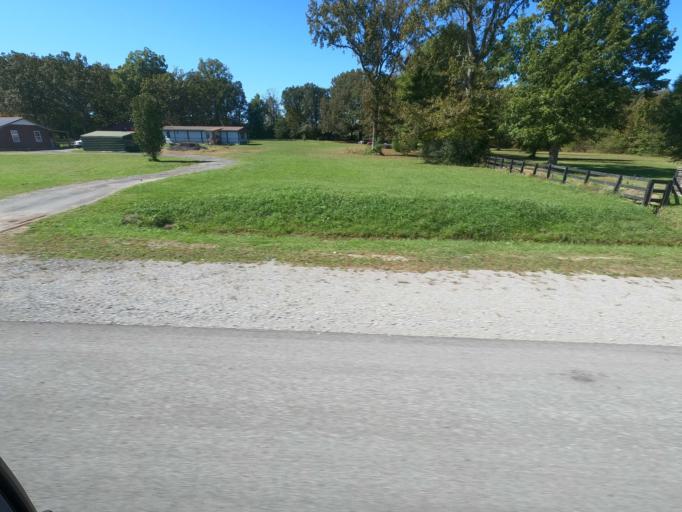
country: US
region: Tennessee
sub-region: Maury County
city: Mount Pleasant
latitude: 35.4355
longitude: -87.2804
